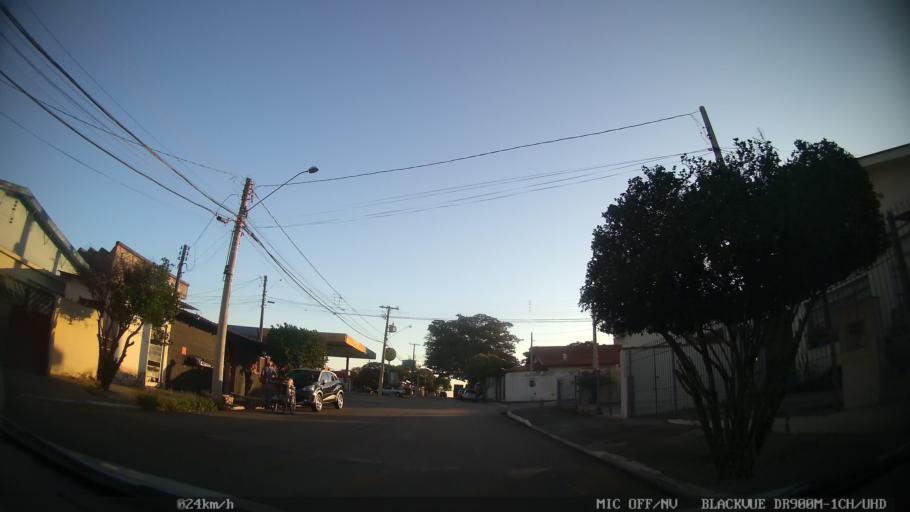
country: BR
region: Sao Paulo
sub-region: Sumare
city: Sumare
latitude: -22.8056
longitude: -47.2221
